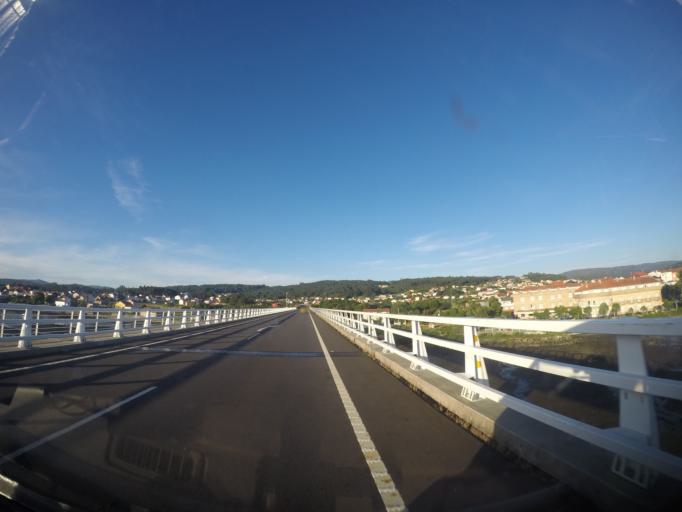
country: ES
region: Galicia
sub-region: Provincia da Coruna
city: Noia
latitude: 42.7956
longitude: -8.8955
